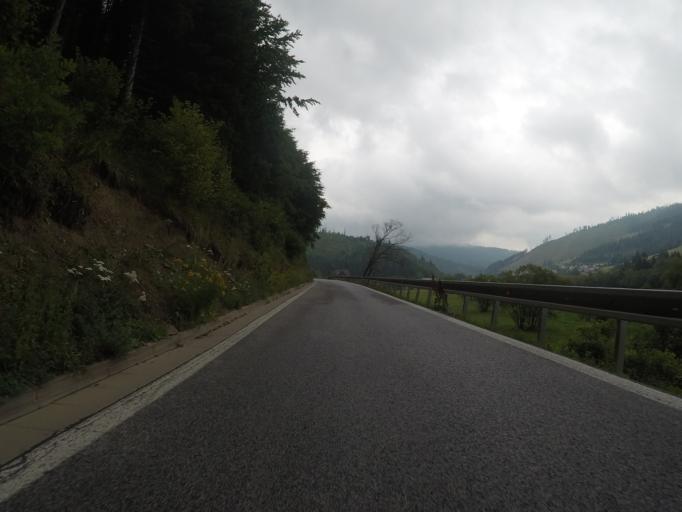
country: SK
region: Kosicky
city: Dobsina
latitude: 48.8556
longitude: 20.3938
